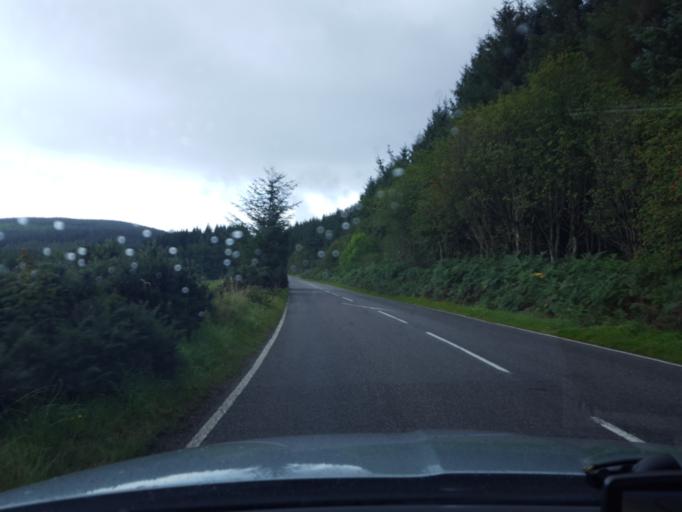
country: GB
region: Scotland
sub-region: Aberdeenshire
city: Banchory
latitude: 57.0151
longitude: -2.3932
